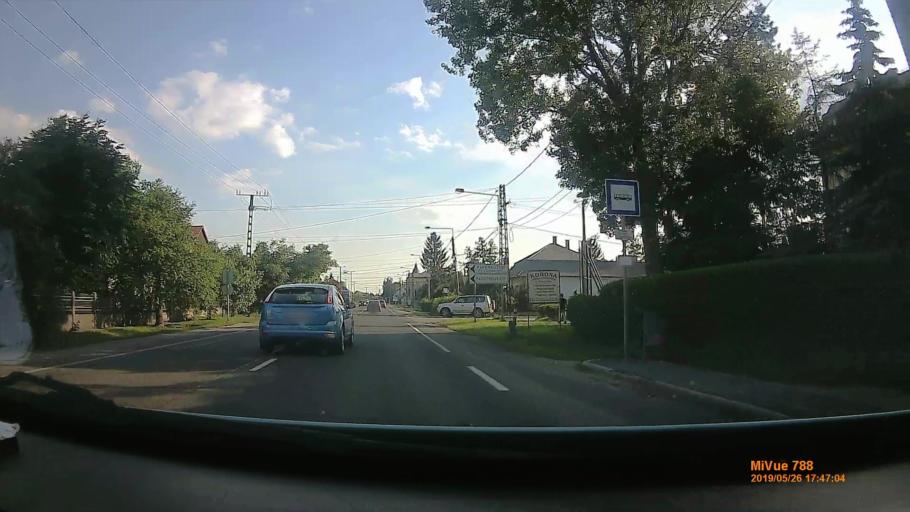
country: HU
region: Borsod-Abauj-Zemplen
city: Szikszo
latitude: 48.2042
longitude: 20.9358
